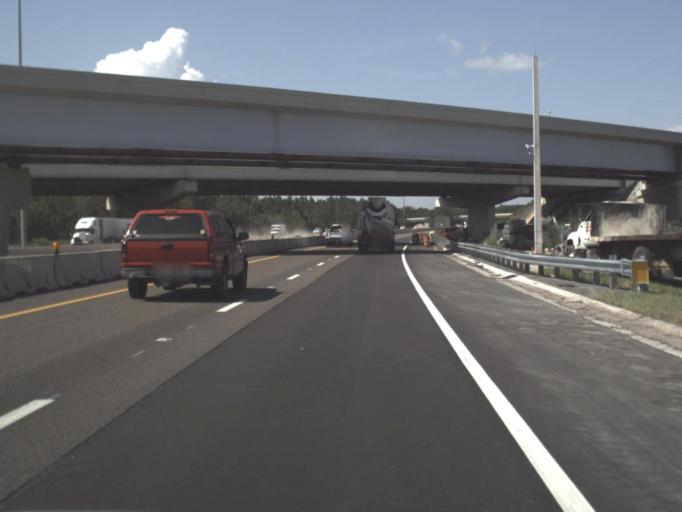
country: US
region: Florida
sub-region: Hillsborough County
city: Pebble Creek
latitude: 28.1656
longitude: -82.3948
